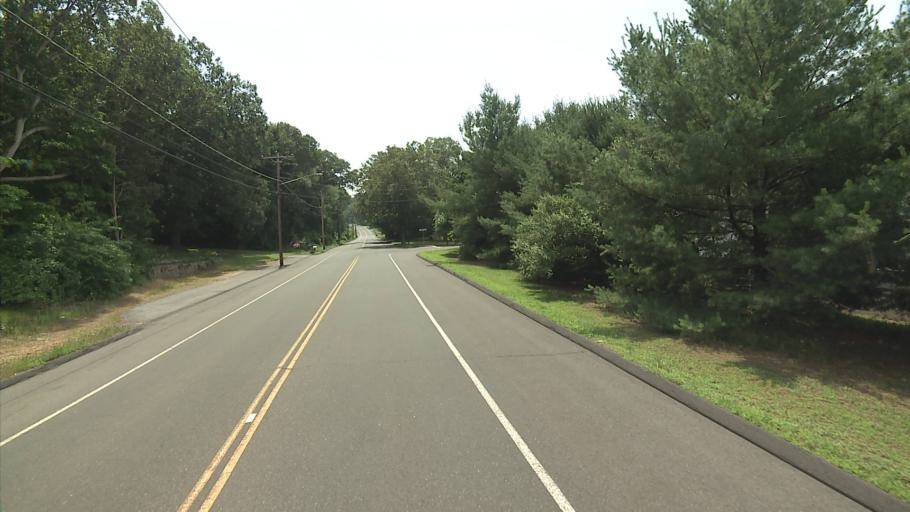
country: US
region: Connecticut
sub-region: New Haven County
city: Madison
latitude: 41.3075
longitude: -72.5921
